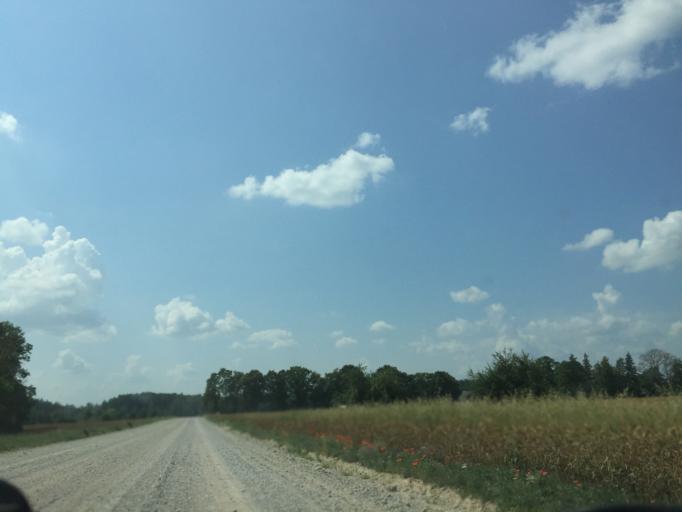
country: LT
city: Zagare
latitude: 56.3912
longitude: 23.3124
